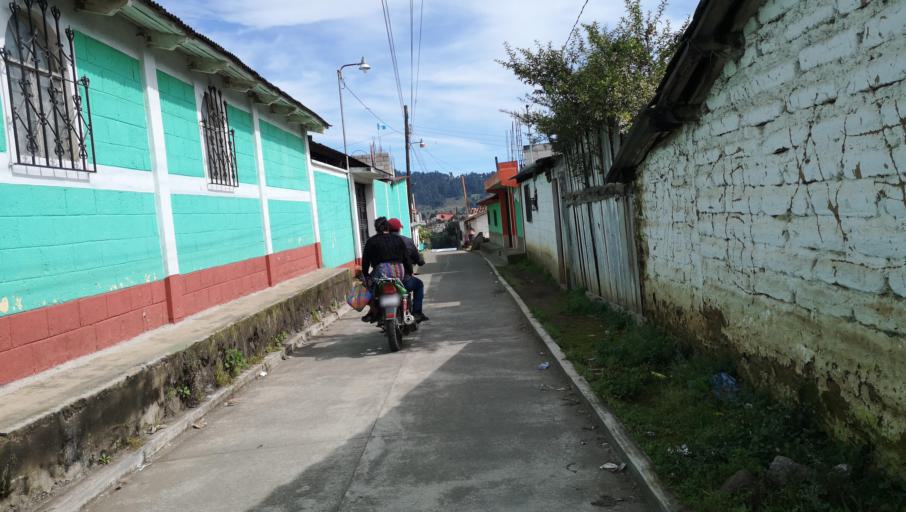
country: GT
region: Quetzaltenango
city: Cantel
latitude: 14.8177
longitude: -91.4393
